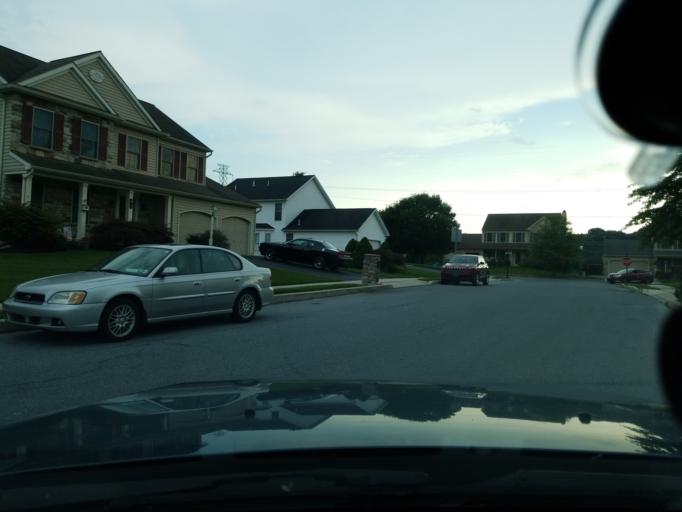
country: US
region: Pennsylvania
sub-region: Dauphin County
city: Hummelstown
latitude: 40.2712
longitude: -76.7261
